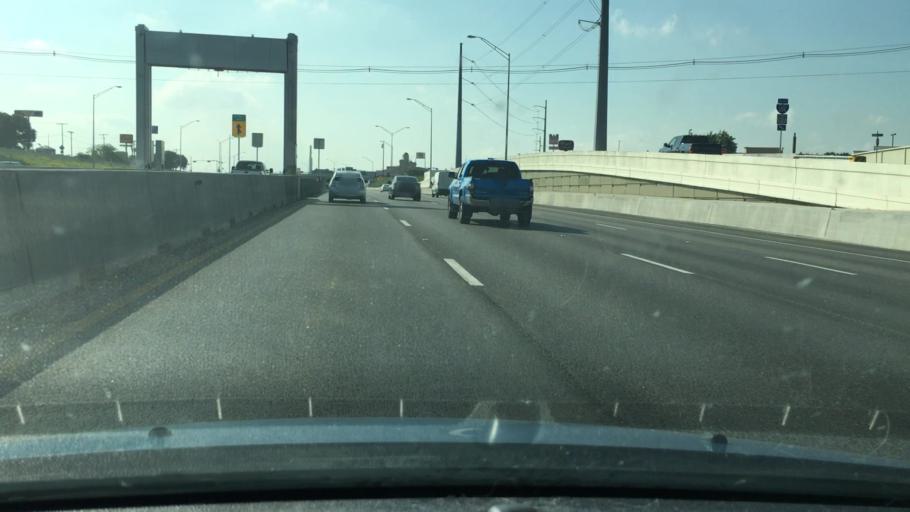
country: US
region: Texas
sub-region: Denton County
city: Lewisville
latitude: 33.0500
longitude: -97.0098
